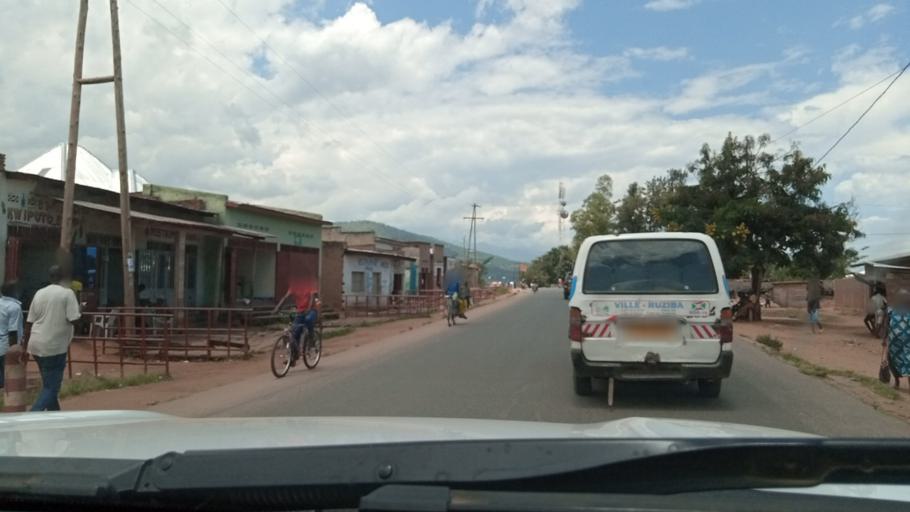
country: BI
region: Bujumbura Mairie
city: Bujumbura
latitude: -3.4695
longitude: 29.3497
